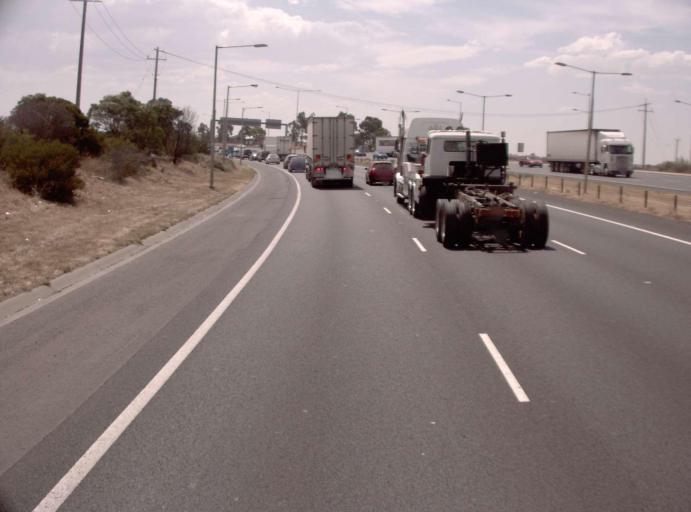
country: AU
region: Victoria
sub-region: Brimbank
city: Sunshine West
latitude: -37.8040
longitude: 144.8068
